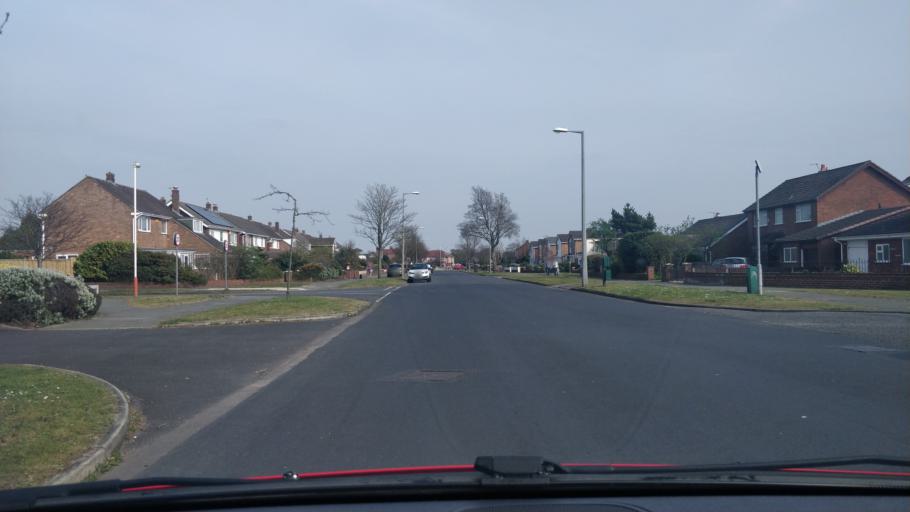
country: GB
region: England
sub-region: Sefton
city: Formby
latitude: 53.5978
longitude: -3.0405
